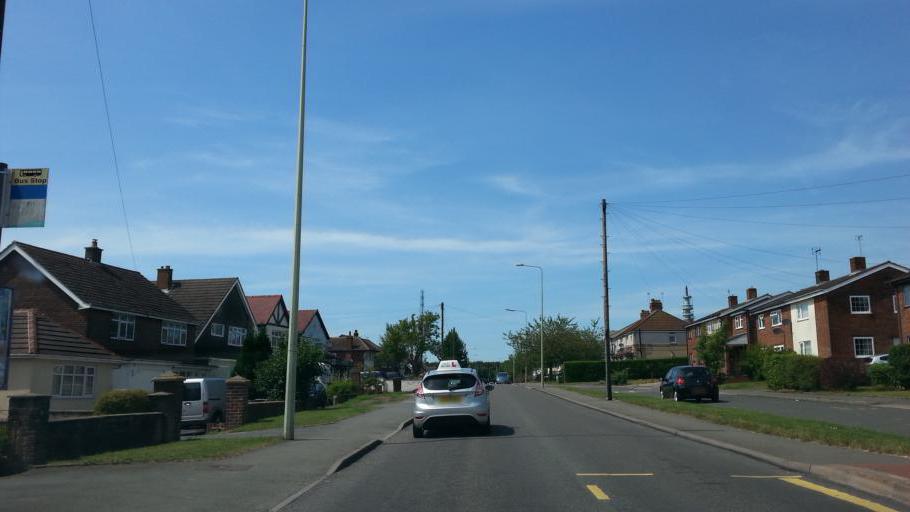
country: GB
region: England
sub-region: Staffordshire
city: Cannock
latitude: 52.7230
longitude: -2.0133
